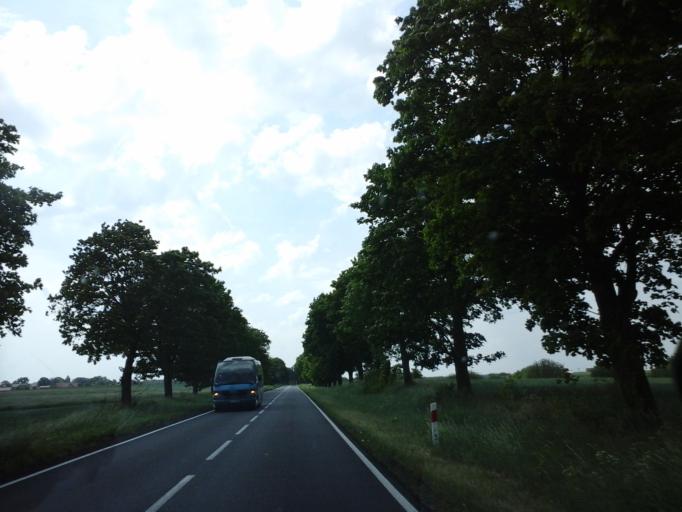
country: PL
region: West Pomeranian Voivodeship
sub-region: Powiat choszczenski
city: Recz
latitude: 53.1895
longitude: 15.6053
